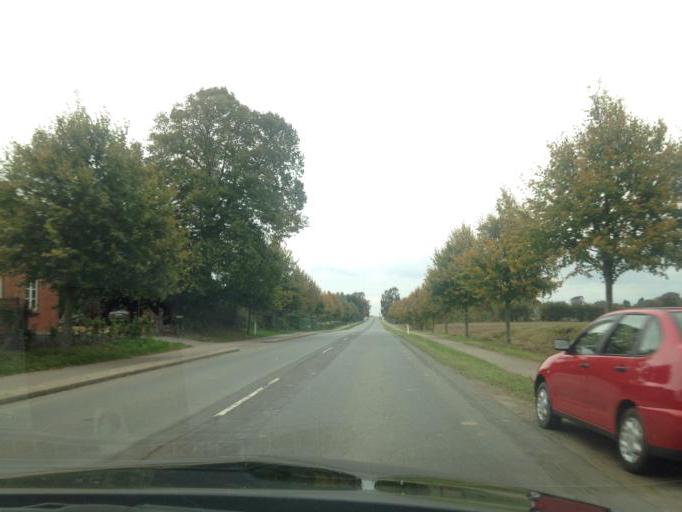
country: DK
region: South Denmark
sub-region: Kolding Kommune
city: Christiansfeld
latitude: 55.3824
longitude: 9.4806
